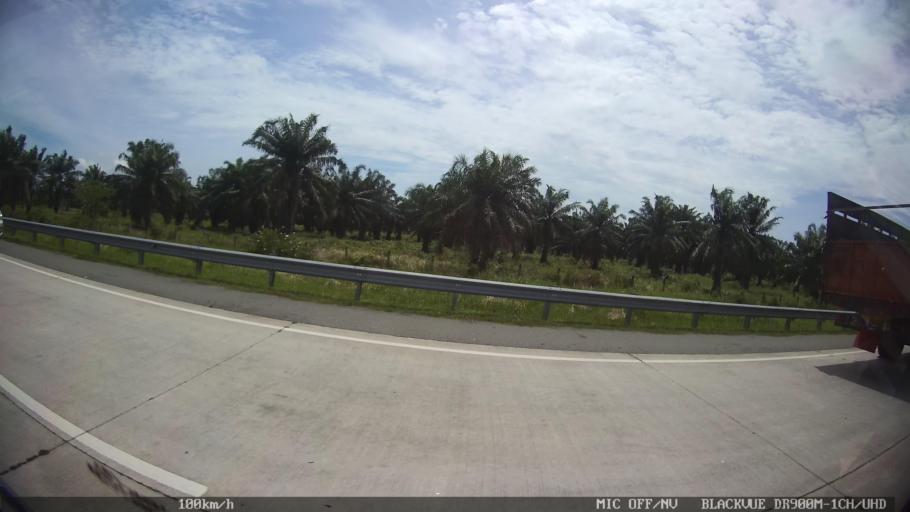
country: ID
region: North Sumatra
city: Percut
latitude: 3.5831
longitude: 98.8459
